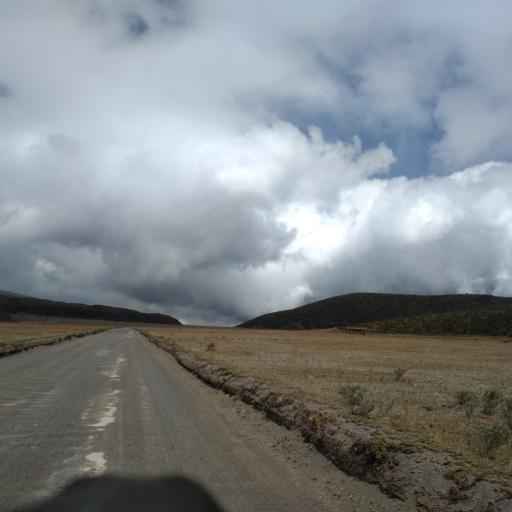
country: EC
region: Pichincha
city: Machachi
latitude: -0.6157
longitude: -78.4734
